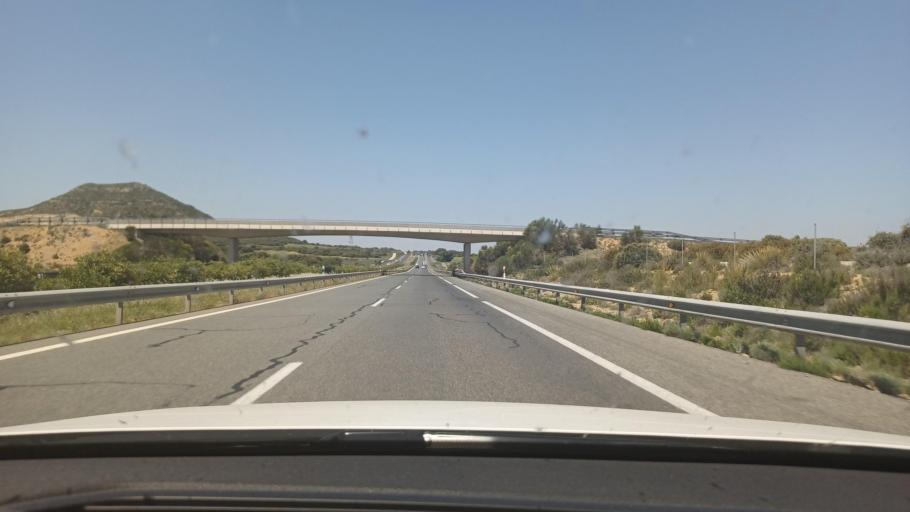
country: ES
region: Castille-La Mancha
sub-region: Provincia de Albacete
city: Corral-Rubio
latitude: 38.8988
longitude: -1.4536
